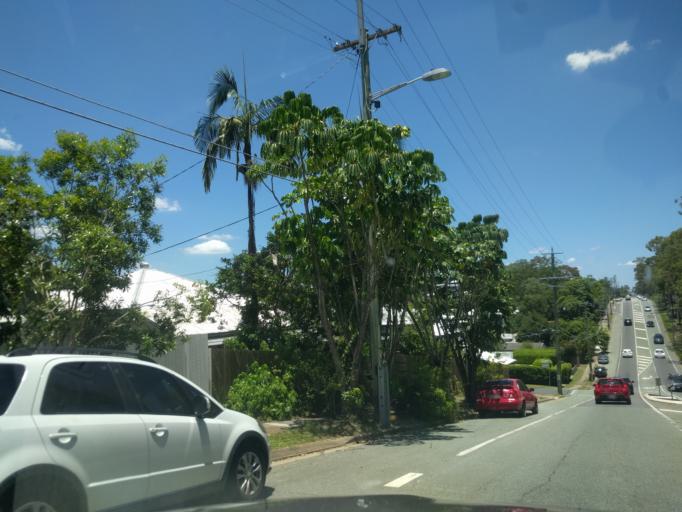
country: AU
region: Queensland
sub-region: Brisbane
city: Toowong
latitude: -27.4719
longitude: 152.9862
